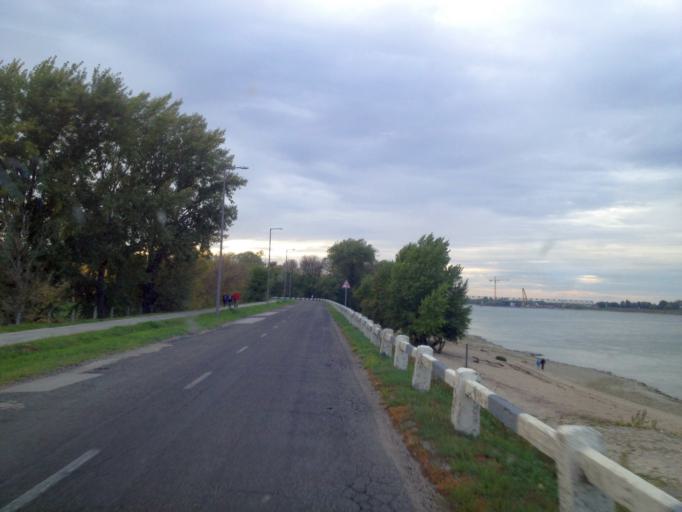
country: HU
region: Komarom-Esztergom
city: Komarom
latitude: 47.7506
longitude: 18.1074
